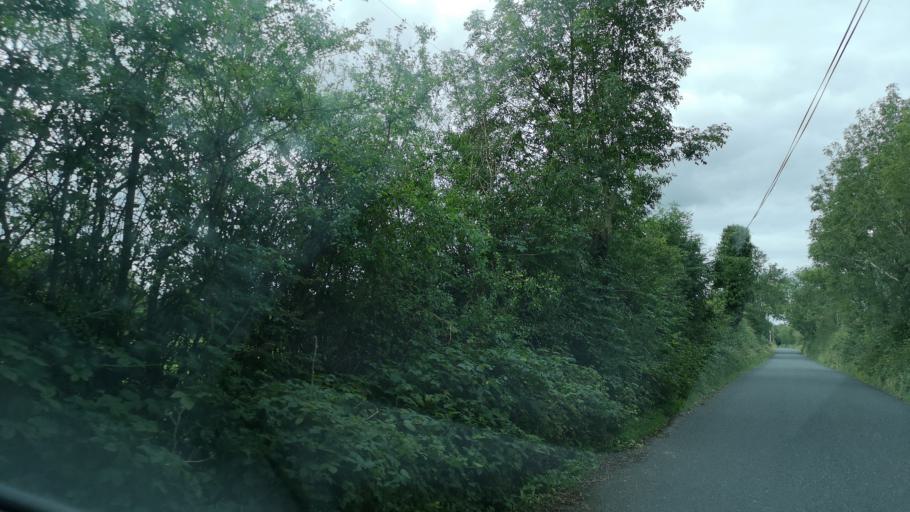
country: IE
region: Connaught
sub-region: County Galway
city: Loughrea
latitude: 53.1590
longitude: -8.4570
